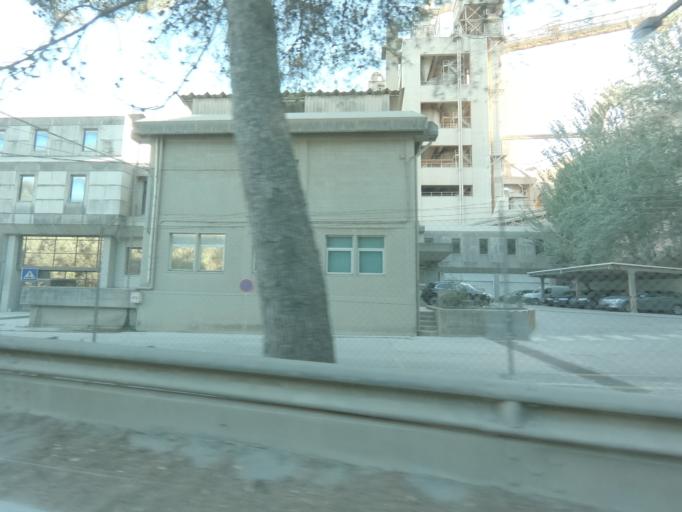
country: PT
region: Setubal
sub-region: Setubal
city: Setubal
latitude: 38.5025
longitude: -8.9362
